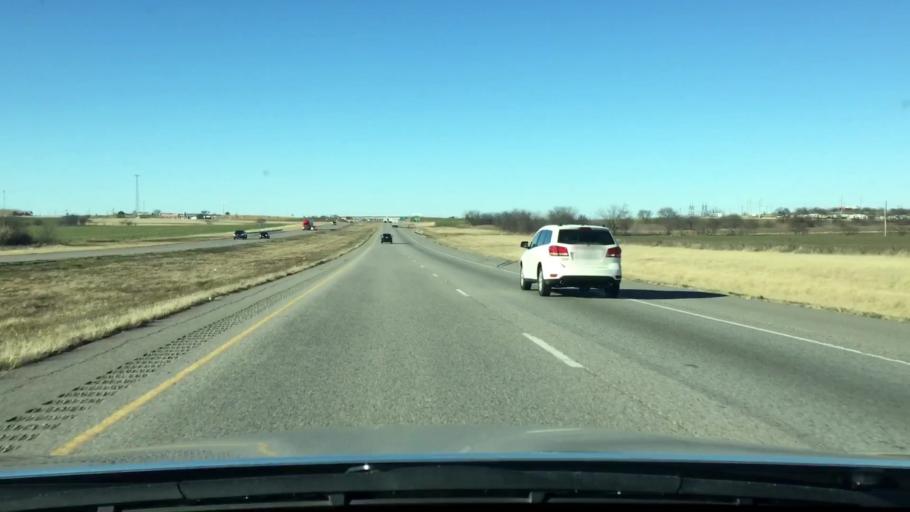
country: US
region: Texas
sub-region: Hill County
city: Itasca
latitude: 32.1444
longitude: -97.1234
